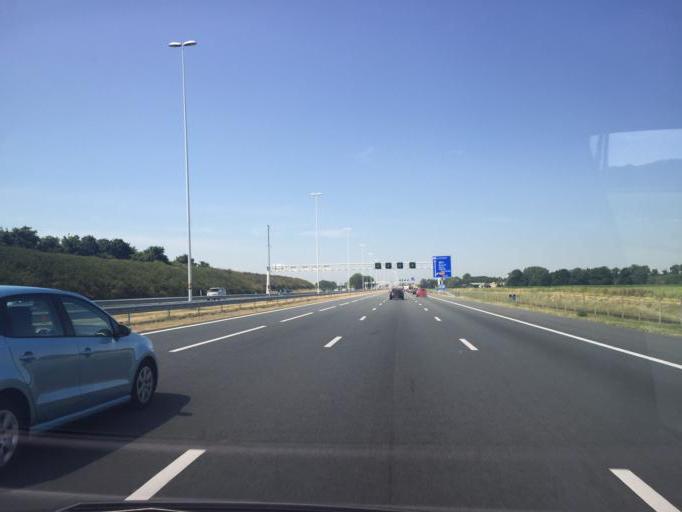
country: NL
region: Utrecht
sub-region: Gemeente Zeist
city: Zeist
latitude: 52.0591
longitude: 5.2306
